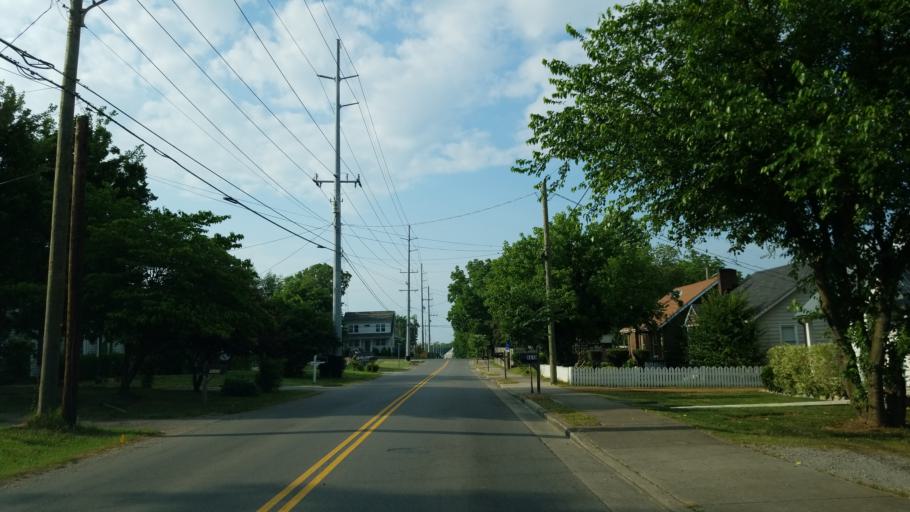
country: US
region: Tennessee
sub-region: Davidson County
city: Nashville
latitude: 36.1365
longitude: -86.7701
